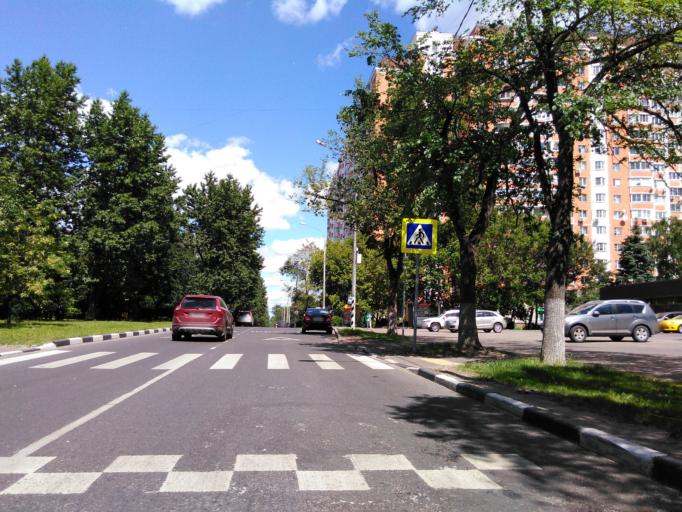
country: RU
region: Moskovskaya
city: Cheremushki
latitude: 55.6716
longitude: 37.5688
